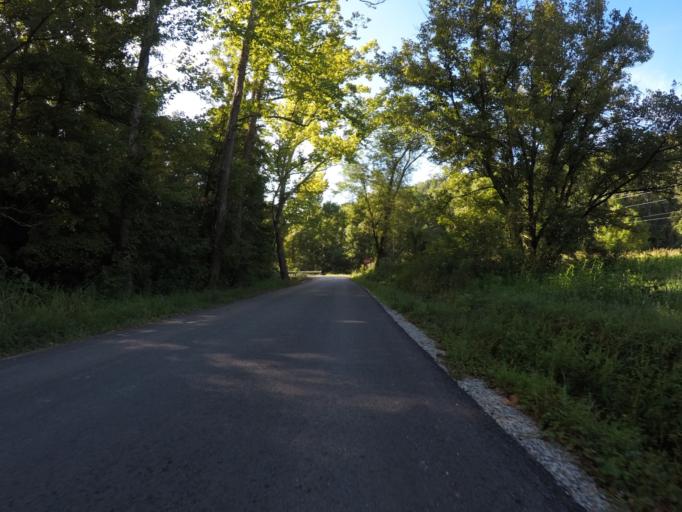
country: US
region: Ohio
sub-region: Lawrence County
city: Burlington
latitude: 38.5057
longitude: -82.5203
